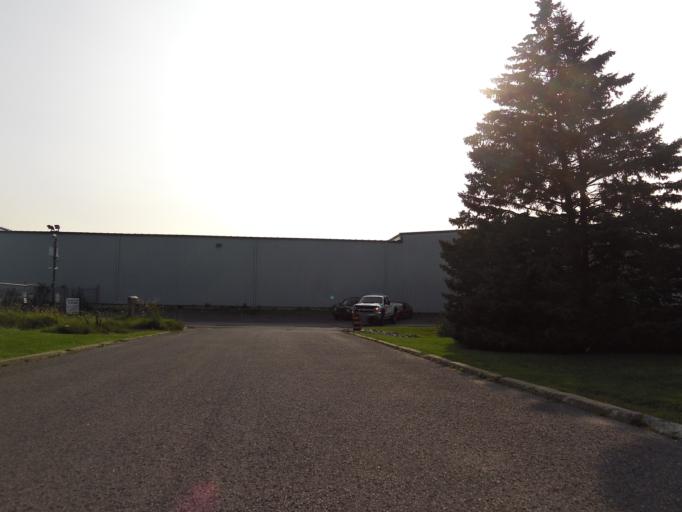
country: CA
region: Ontario
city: Ottawa
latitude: 45.3353
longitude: -75.7117
